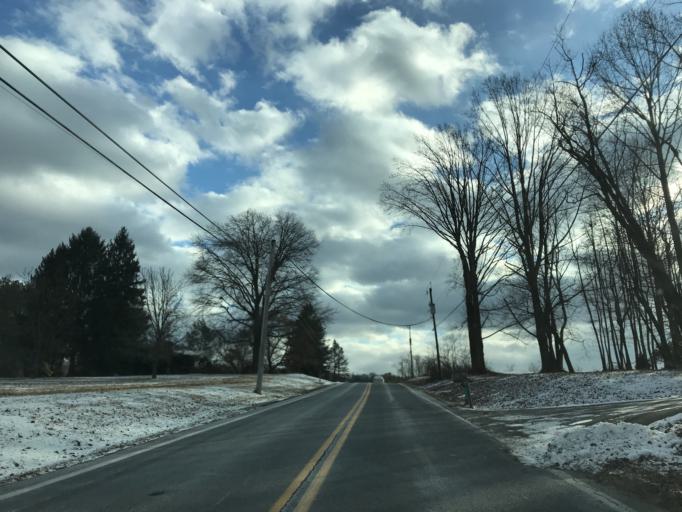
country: US
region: Maryland
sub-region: Harford County
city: Bel Air North
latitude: 39.6551
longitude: -76.3830
